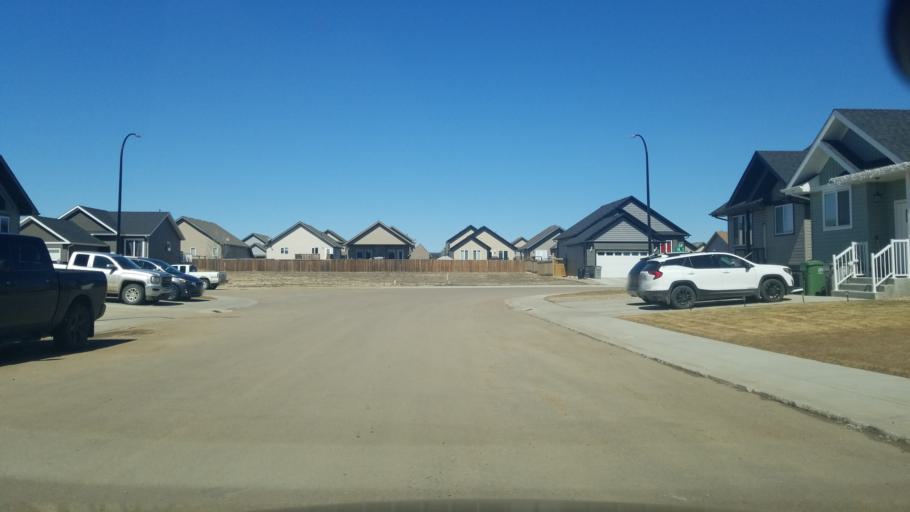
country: CA
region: Saskatchewan
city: Lloydminster
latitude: 53.2502
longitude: -110.0199
